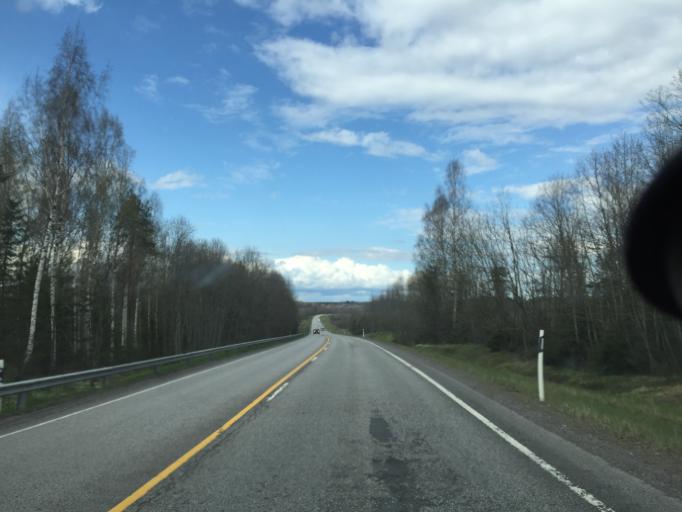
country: FI
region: Uusimaa
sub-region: Helsinki
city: Lohja
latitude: 60.1868
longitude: 24.0087
